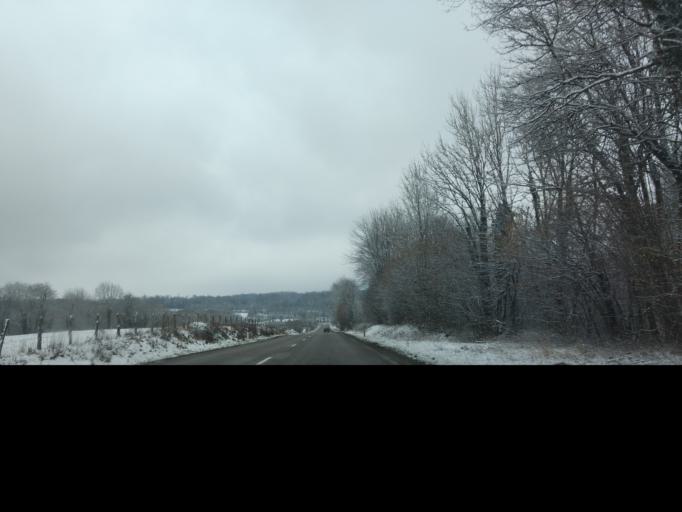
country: FR
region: Franche-Comte
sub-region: Departement du Jura
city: Arbois
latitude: 46.8059
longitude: 5.8209
